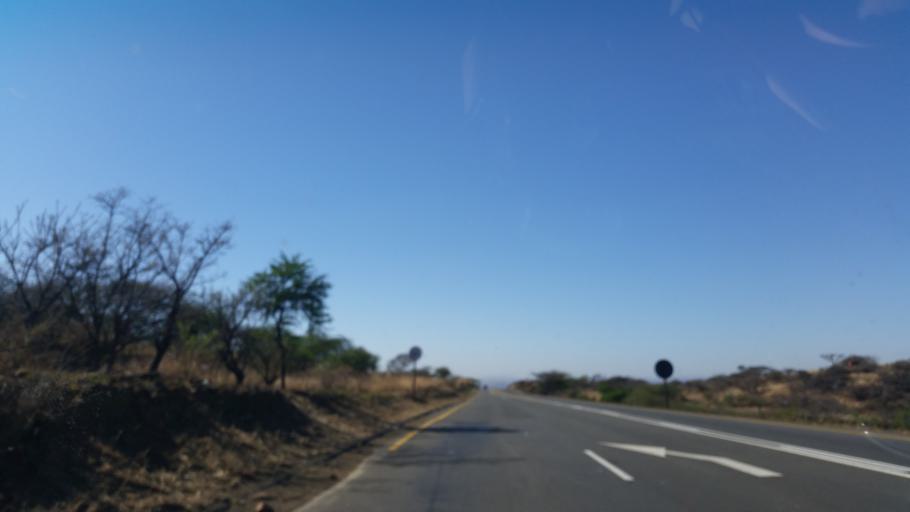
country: ZA
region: KwaZulu-Natal
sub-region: uThukela District Municipality
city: Ladysmith
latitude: -28.6944
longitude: 29.7656
